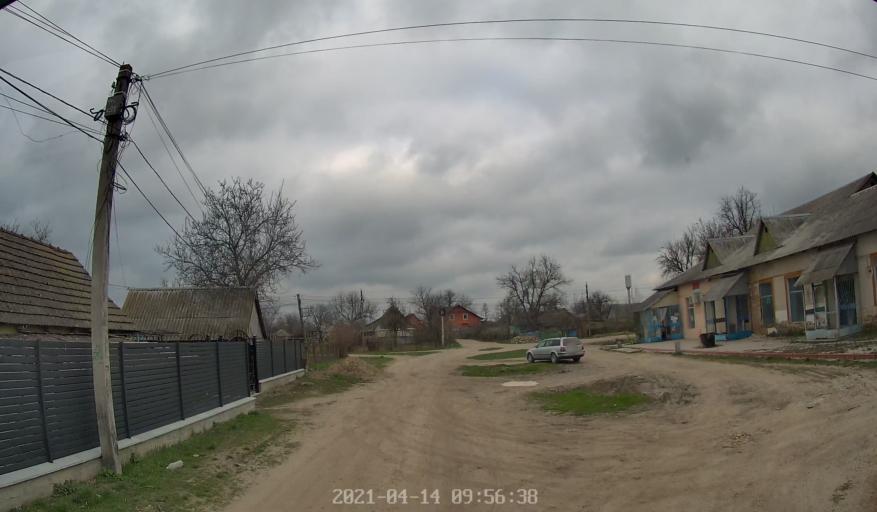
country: MD
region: Chisinau
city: Vadul lui Voda
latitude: 47.1406
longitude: 29.1246
